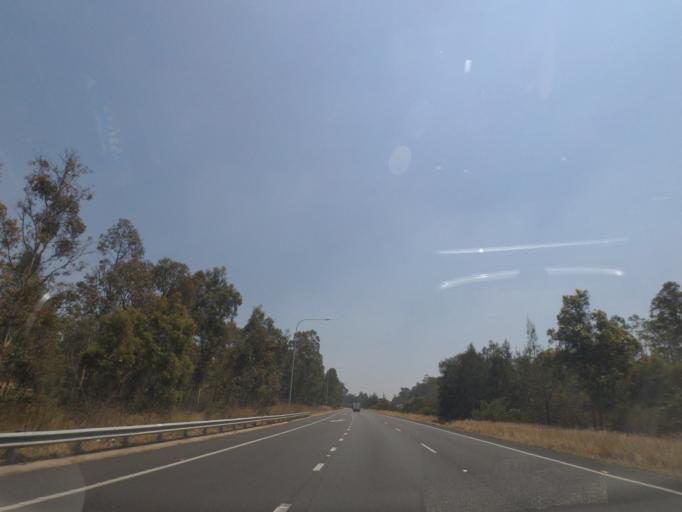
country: AU
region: New South Wales
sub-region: Newcastle
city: Beresfield
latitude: -32.8331
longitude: 151.6347
